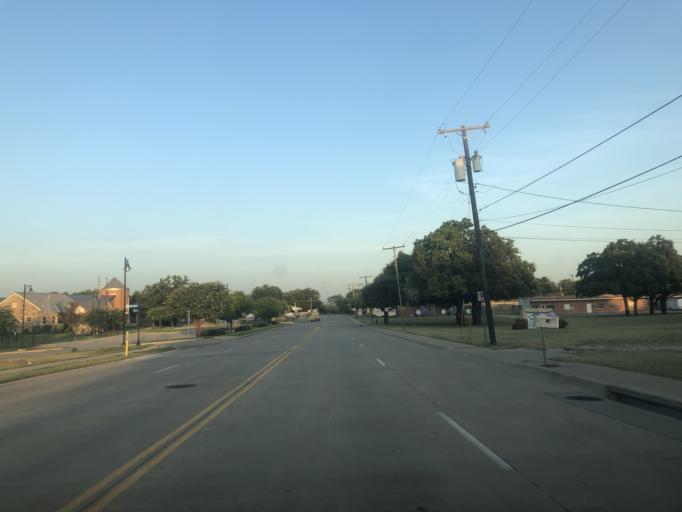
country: US
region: Texas
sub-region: Tarrant County
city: Lake Worth
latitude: 32.8100
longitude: -97.4405
